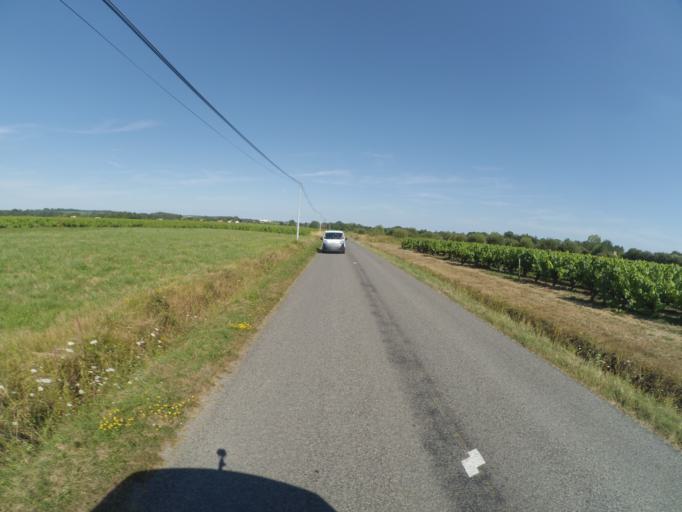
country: FR
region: Pays de la Loire
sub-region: Departement de la Loire-Atlantique
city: Le Pallet
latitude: 47.1577
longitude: -1.3172
